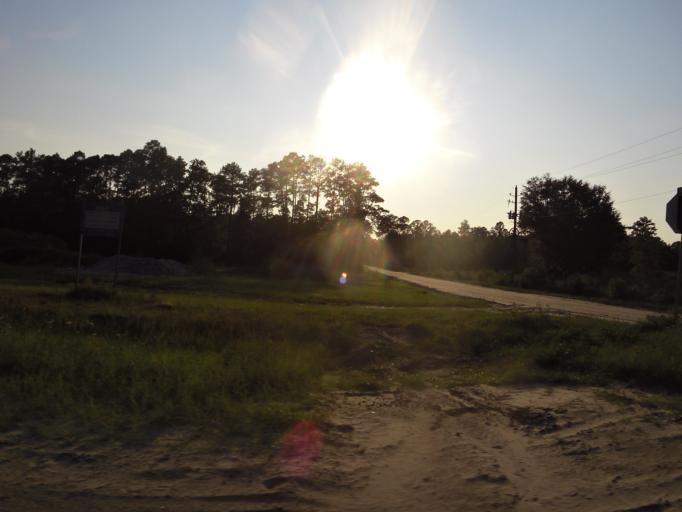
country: US
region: Florida
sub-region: Nassau County
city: Hilliard
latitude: 30.5198
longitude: -82.0374
